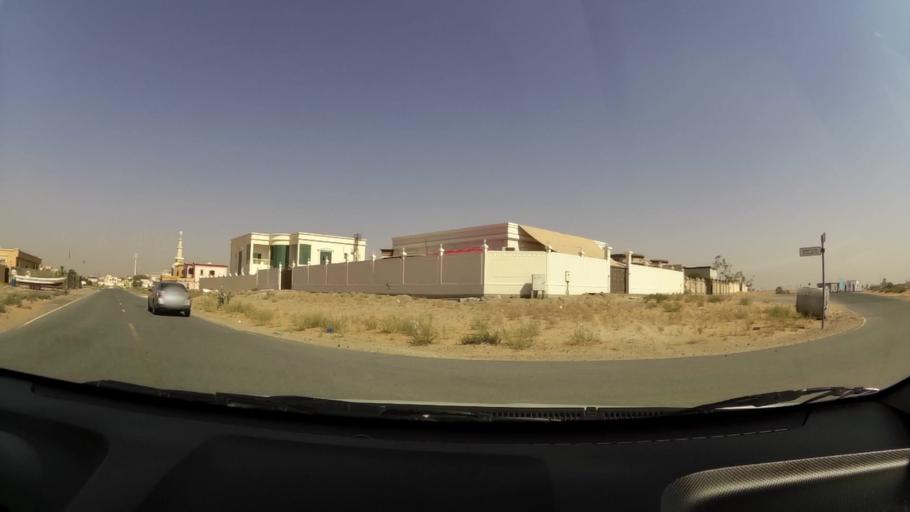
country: AE
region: Umm al Qaywayn
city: Umm al Qaywayn
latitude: 25.4762
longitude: 55.6093
